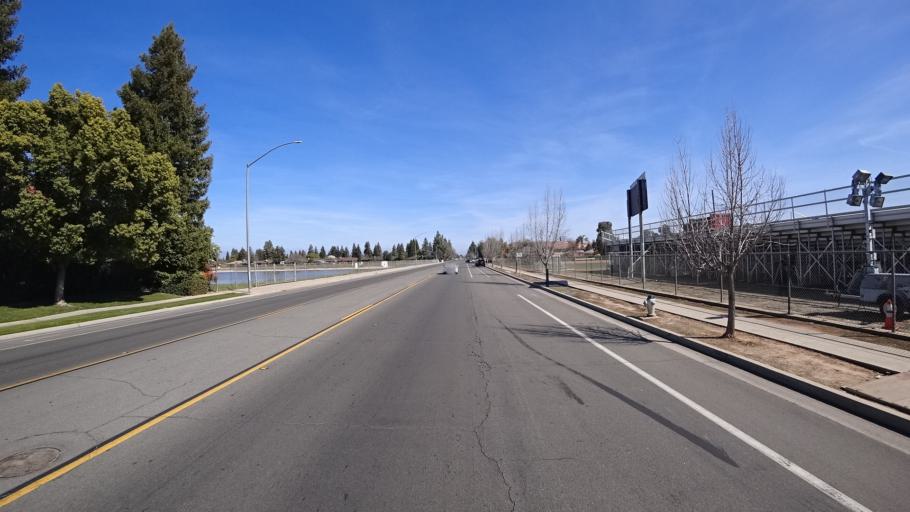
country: US
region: California
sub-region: Fresno County
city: Clovis
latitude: 36.8448
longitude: -119.7551
